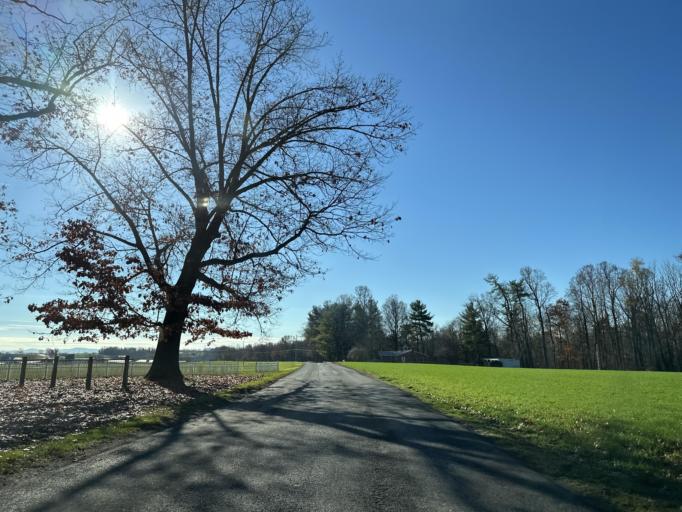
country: US
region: Virginia
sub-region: Rockingham County
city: Dayton
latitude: 38.4442
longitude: -78.9903
